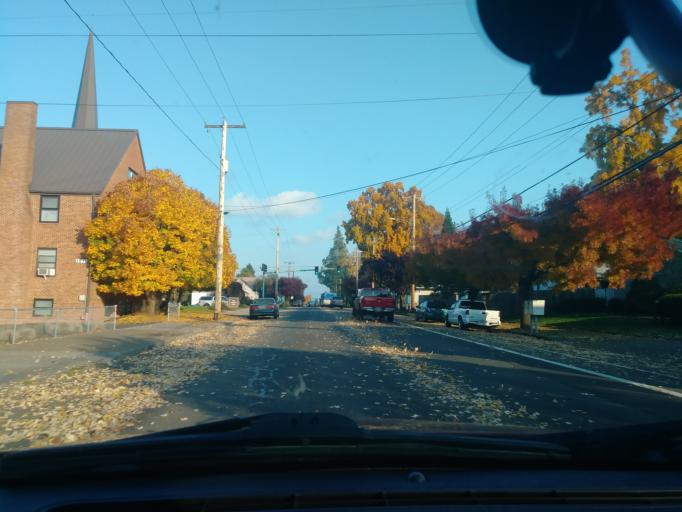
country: US
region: Oregon
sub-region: Washington County
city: Forest Grove
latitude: 45.5184
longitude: -123.1077
